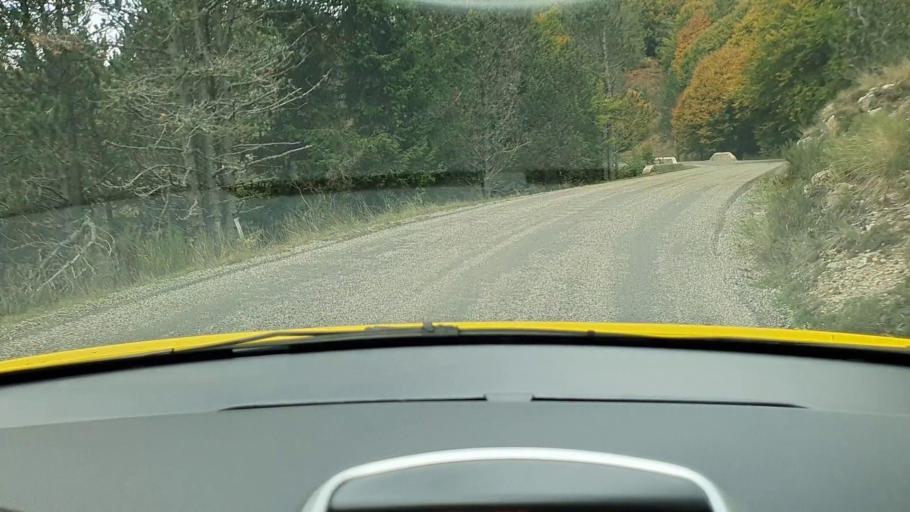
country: FR
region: Languedoc-Roussillon
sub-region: Departement du Gard
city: Valleraugue
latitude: 44.0690
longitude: 3.5420
